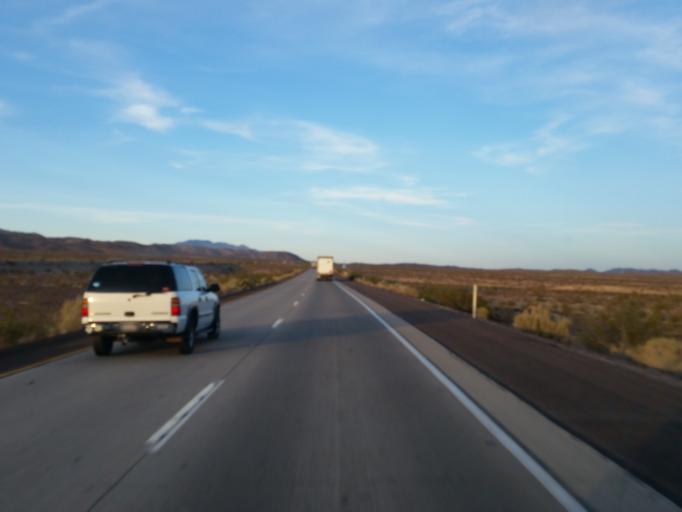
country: US
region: California
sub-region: San Bernardino County
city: Twentynine Palms
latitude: 34.7208
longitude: -115.9763
